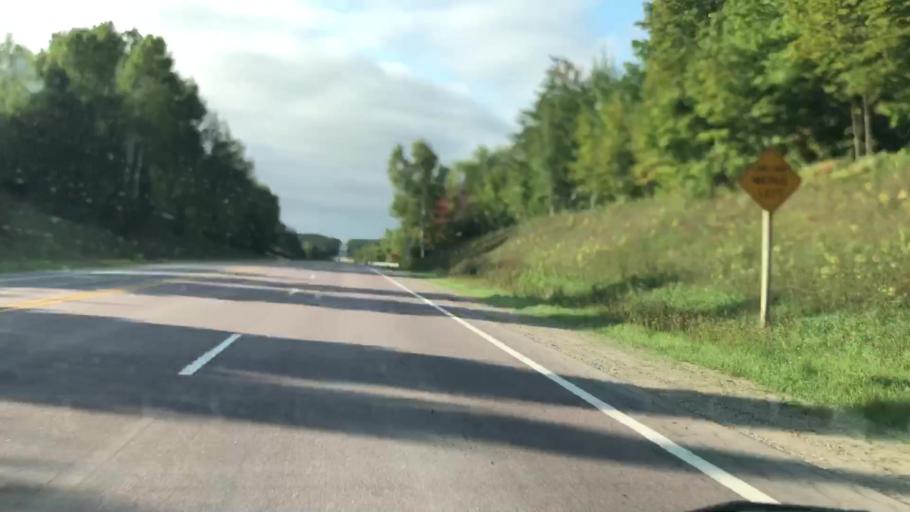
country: US
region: Michigan
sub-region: Luce County
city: Newberry
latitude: 46.3060
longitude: -85.5677
